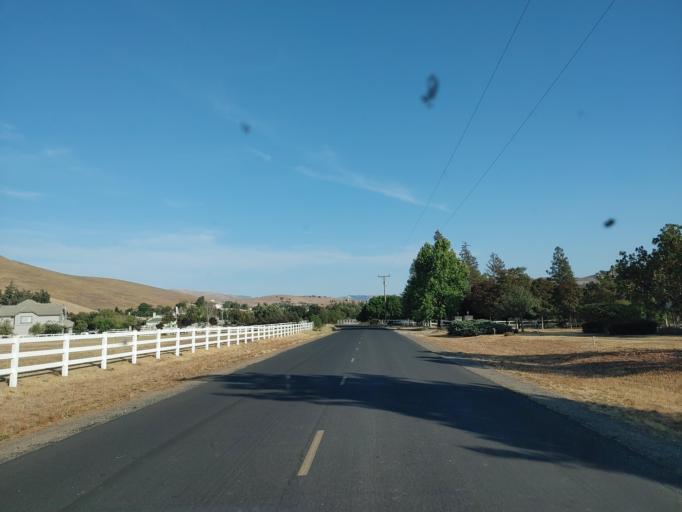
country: US
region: California
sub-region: San Benito County
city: Ridgemark
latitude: 36.8008
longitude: -121.3281
